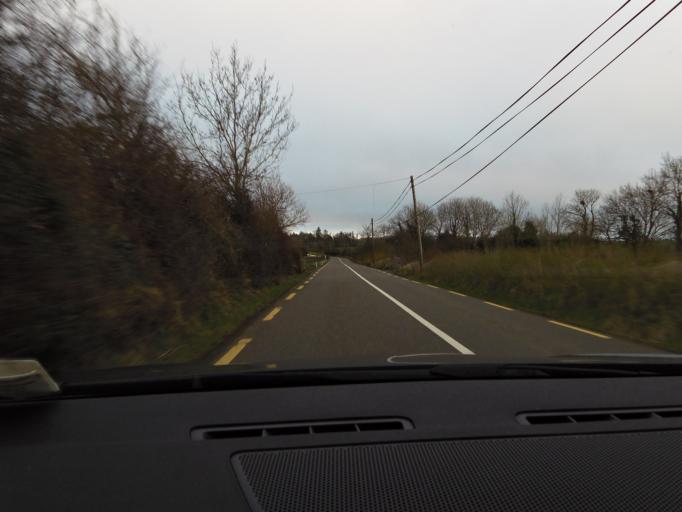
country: IE
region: Connaught
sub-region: Sligo
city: Ballymote
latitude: 54.0054
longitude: -8.5445
